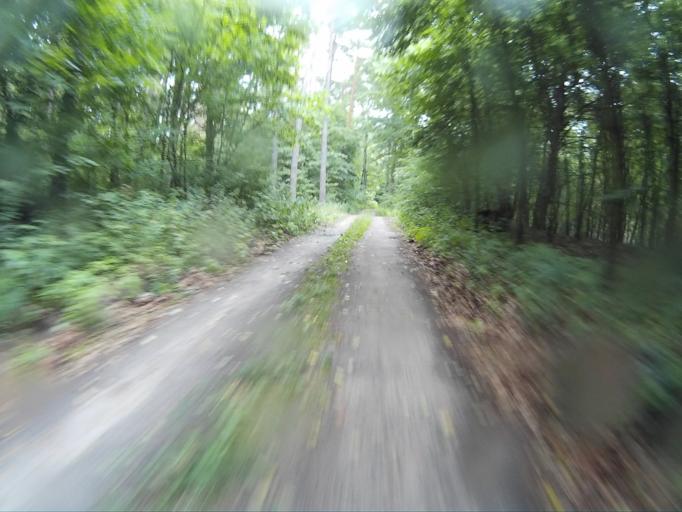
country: PL
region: Kujawsko-Pomorskie
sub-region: Powiat tucholski
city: Tuchola
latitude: 53.5308
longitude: 17.8751
